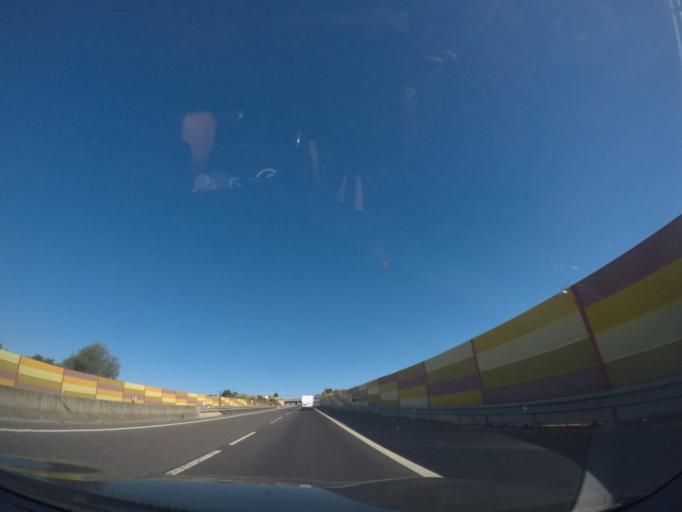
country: PT
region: Faro
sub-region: Lagoa
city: Lagoa
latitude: 37.1469
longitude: -8.4206
